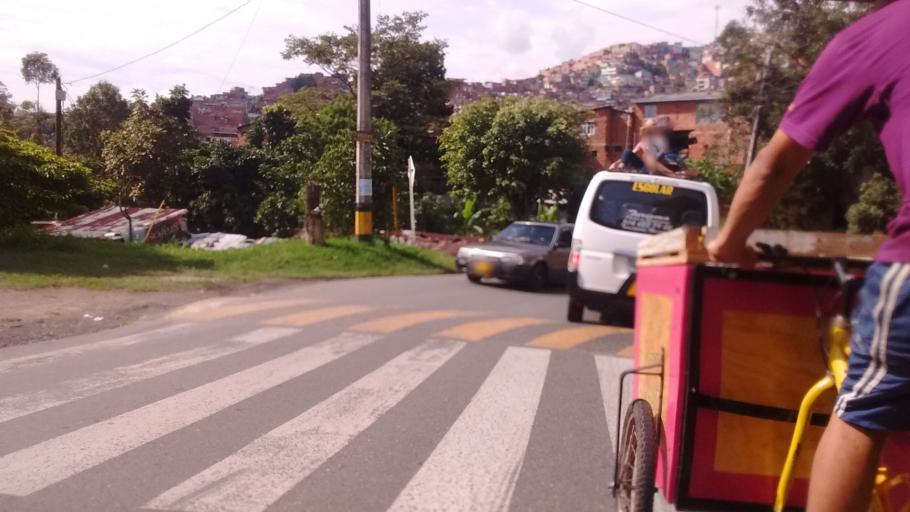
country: CO
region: Antioquia
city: Medellin
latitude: 6.2535
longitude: -75.6213
